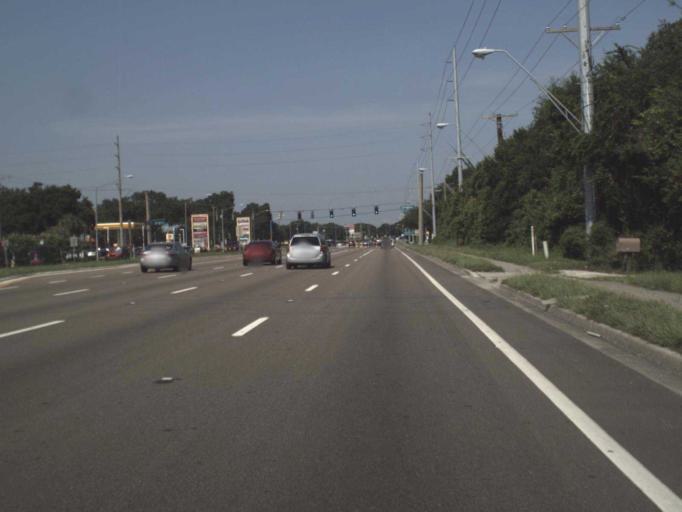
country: US
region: Florida
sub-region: Hillsborough County
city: Brandon
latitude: 27.9379
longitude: -82.3127
